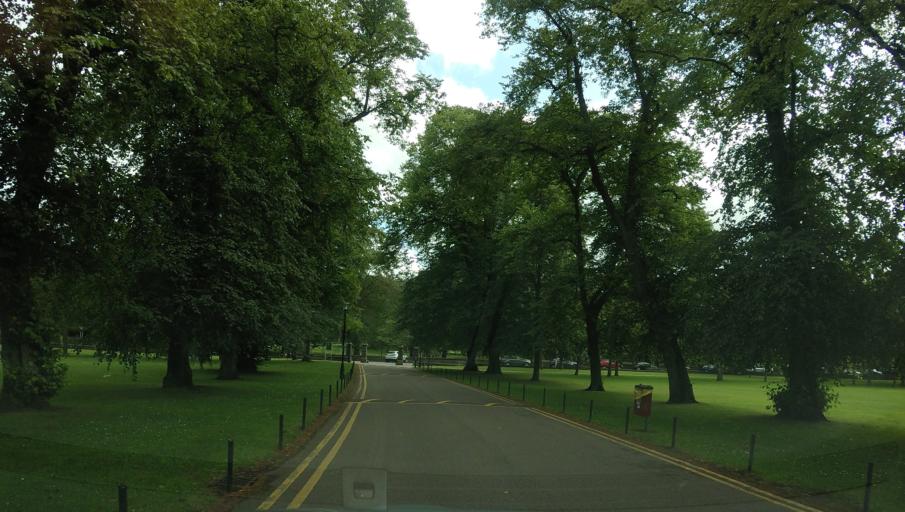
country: GB
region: Scotland
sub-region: Aberdeen City
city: Aberdeen
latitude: 57.1534
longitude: -2.1233
